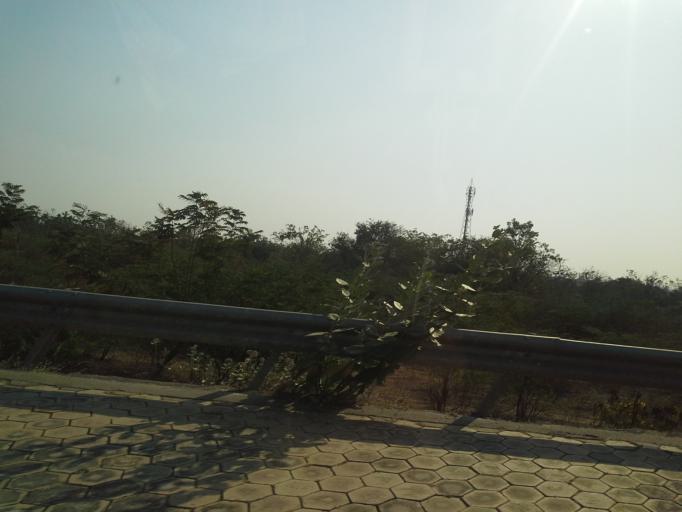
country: IN
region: Telangana
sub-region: Rangareddi
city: Sriramnagar
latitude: 17.2447
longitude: 78.3845
